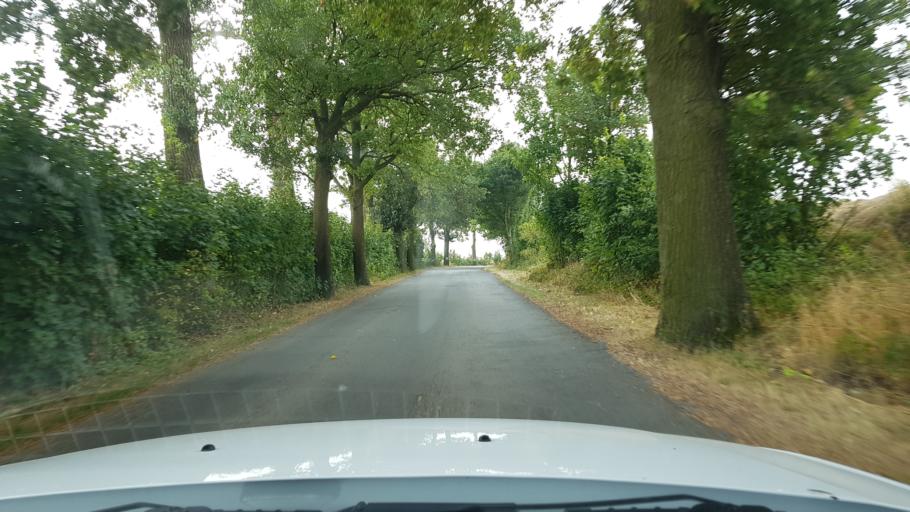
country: PL
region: West Pomeranian Voivodeship
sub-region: Powiat gryfinski
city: Moryn
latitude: 52.8847
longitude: 14.3785
